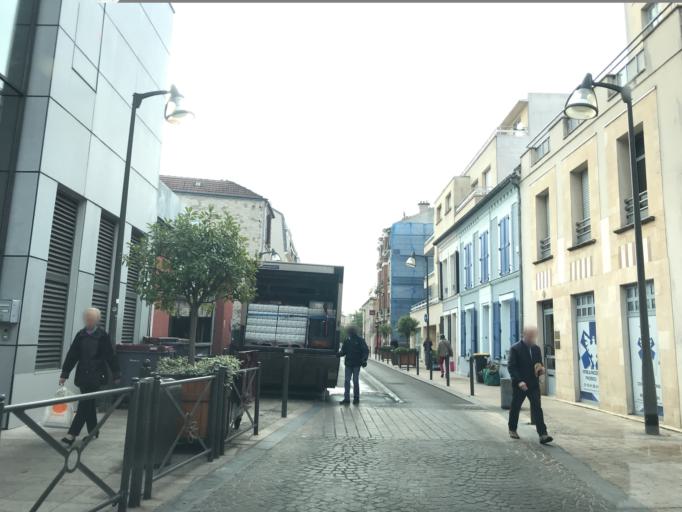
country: FR
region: Ile-de-France
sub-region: Departement du Val-de-Marne
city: Le Perreux-sur-Marne
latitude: 48.8415
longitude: 2.5045
